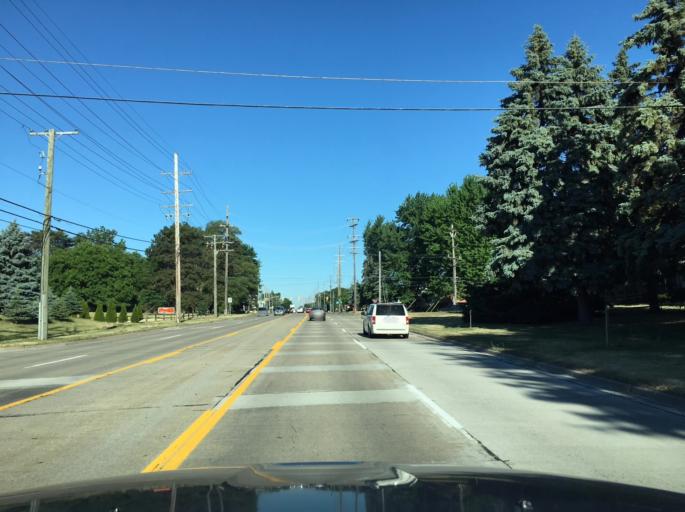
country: US
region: Michigan
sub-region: Macomb County
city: Fraser
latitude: 42.5385
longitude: -82.9665
